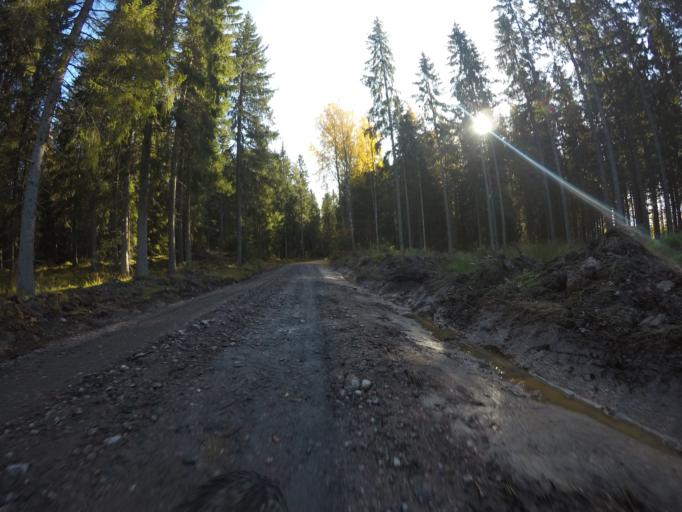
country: SE
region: Vaestmanland
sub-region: Kungsors Kommun
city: Kungsoer
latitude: 59.3103
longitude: 16.0992
